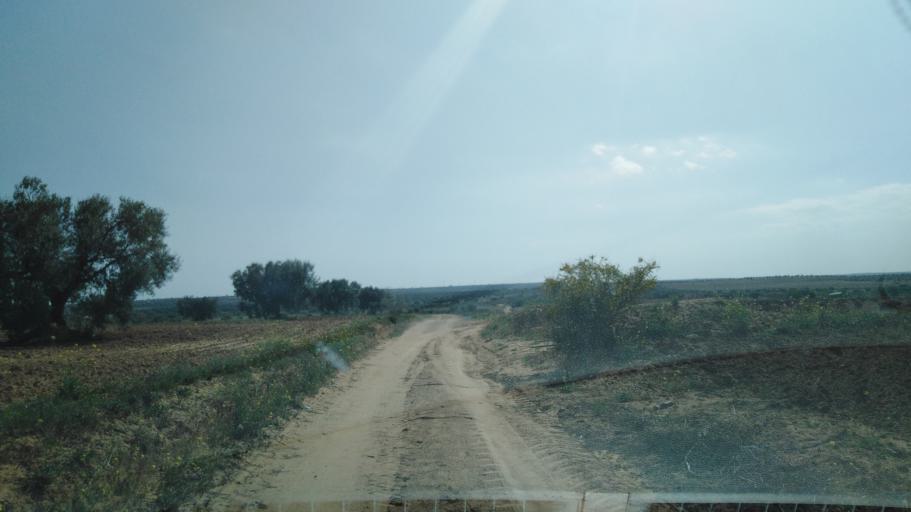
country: TN
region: Safaqis
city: Bi'r `Ali Bin Khalifah
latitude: 34.7839
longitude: 10.3687
